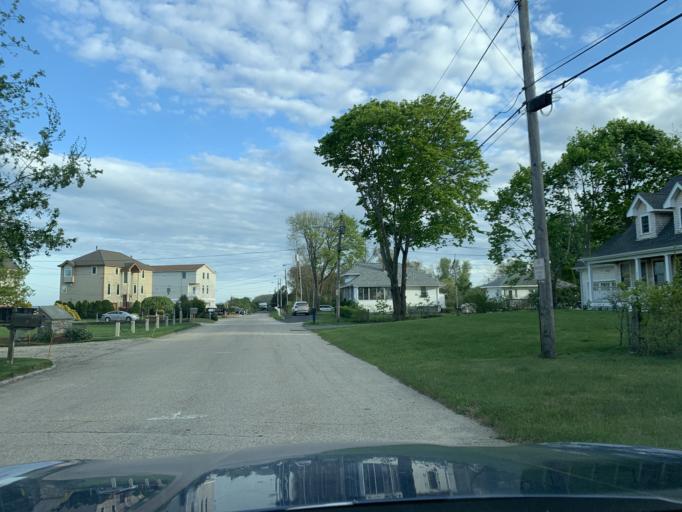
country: US
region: Rhode Island
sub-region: Kent County
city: Warwick
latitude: 41.6613
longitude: -71.4113
